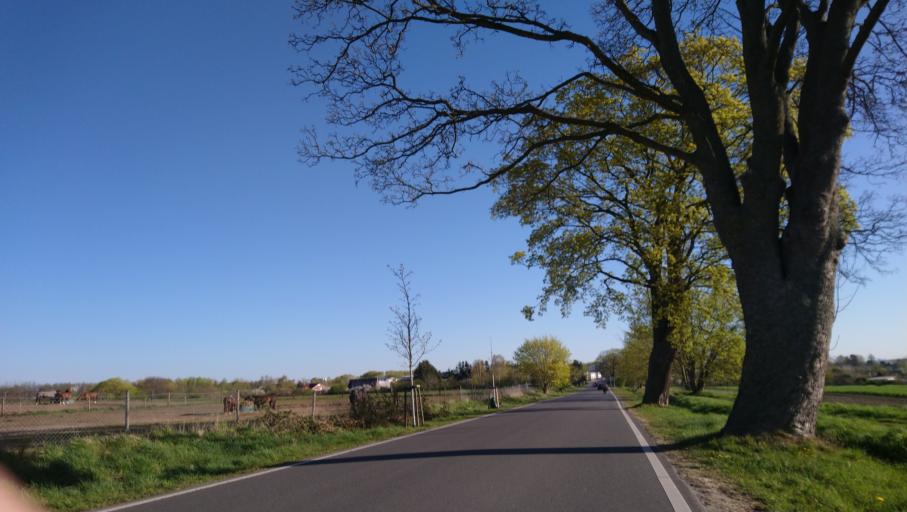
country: DE
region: Mecklenburg-Vorpommern
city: Papendorf
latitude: 54.0604
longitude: 12.1283
